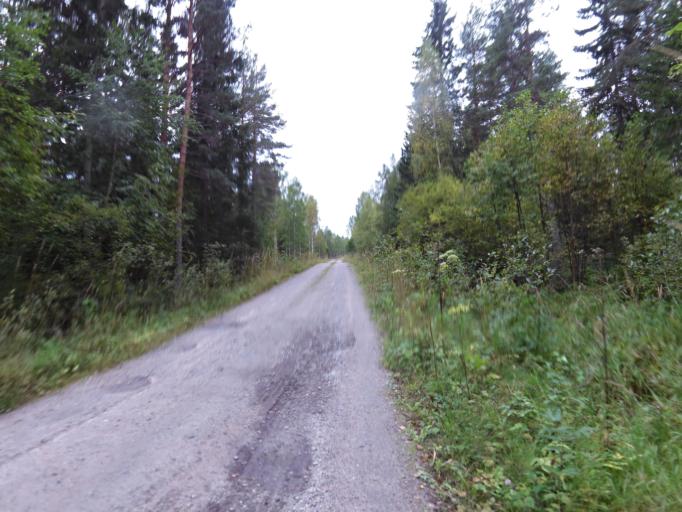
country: SE
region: Gaevleborg
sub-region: Gavle Kommun
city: Valbo
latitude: 60.7373
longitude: 17.0536
